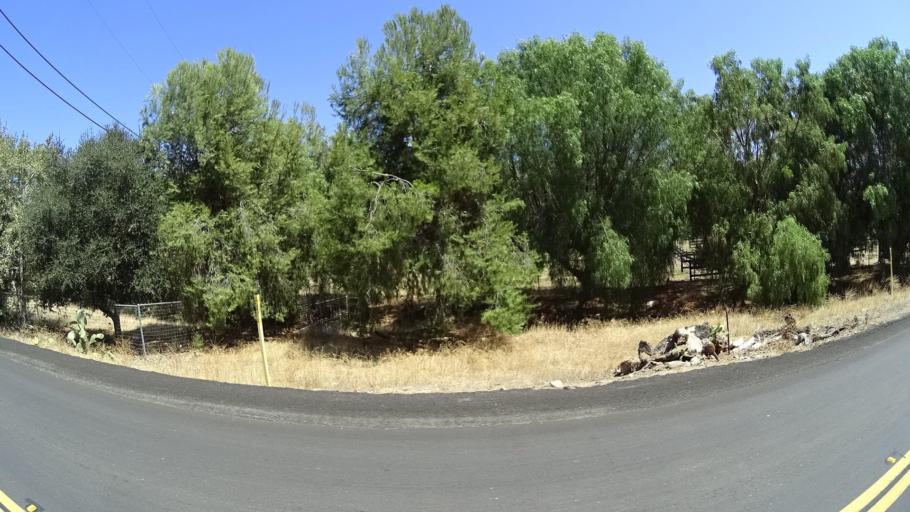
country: US
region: California
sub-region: San Diego County
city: Rainbow
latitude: 33.3460
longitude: -117.1353
